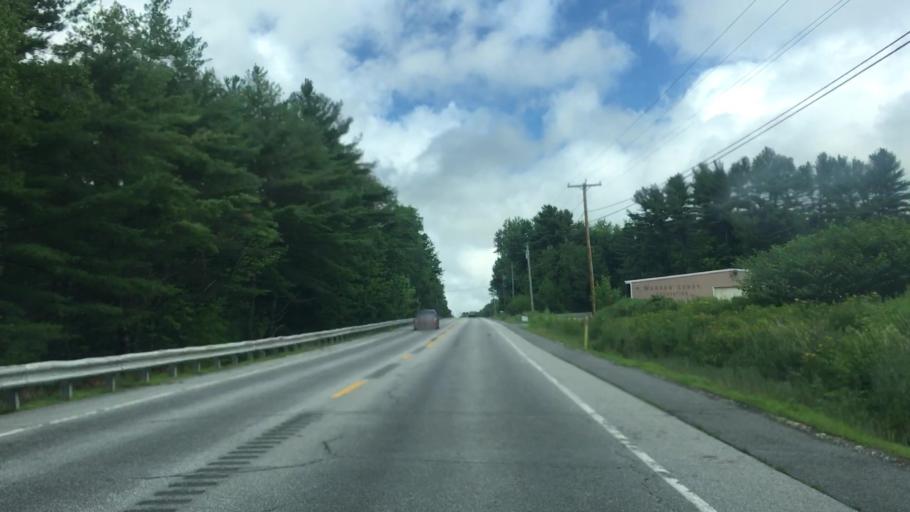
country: US
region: Maine
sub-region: Kennebec County
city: Farmingdale
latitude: 44.2583
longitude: -69.7649
